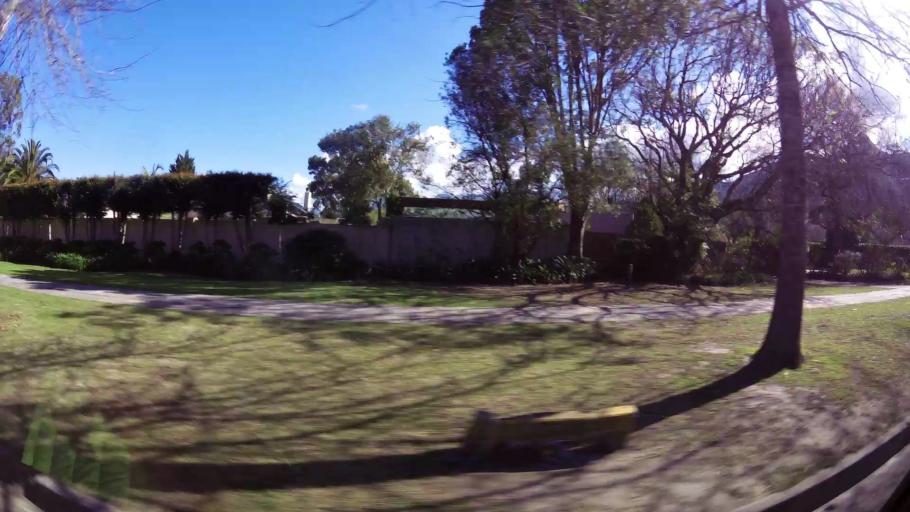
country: ZA
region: Western Cape
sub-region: Eden District Municipality
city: George
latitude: -33.9496
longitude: 22.4625
